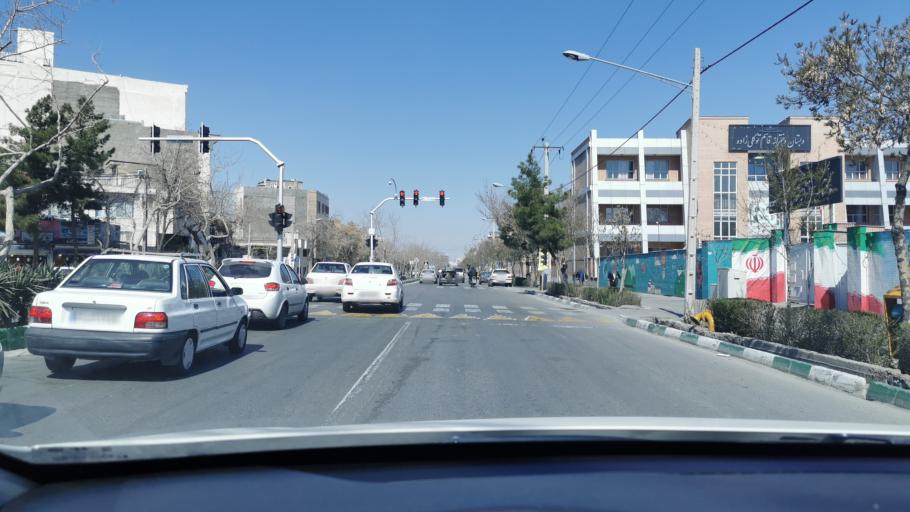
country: IR
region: Razavi Khorasan
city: Mashhad
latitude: 36.2763
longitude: 59.5766
